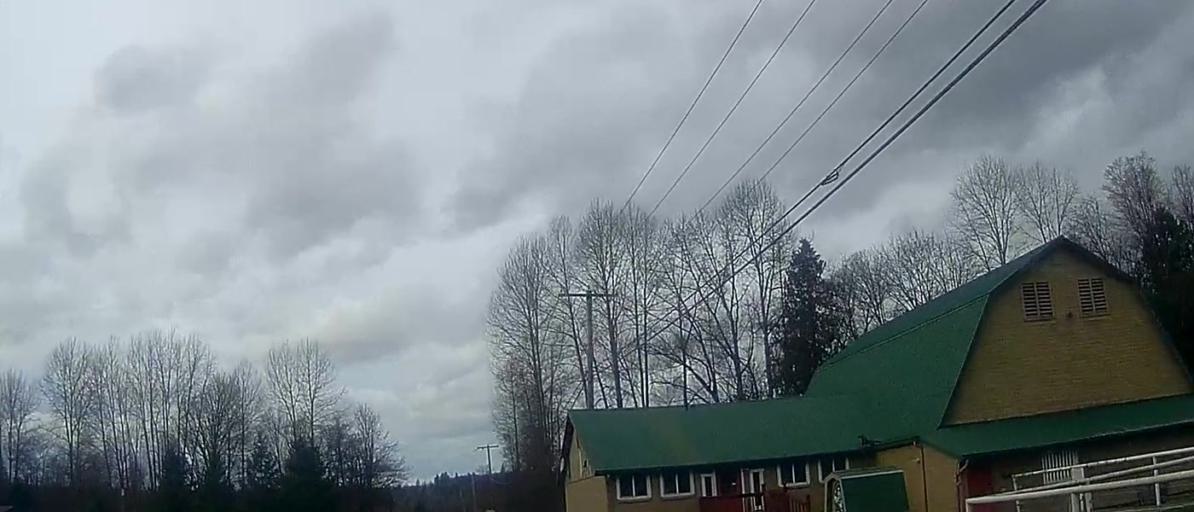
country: US
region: Washington
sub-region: Skagit County
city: Sedro-Woolley
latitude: 48.5835
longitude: -122.2732
